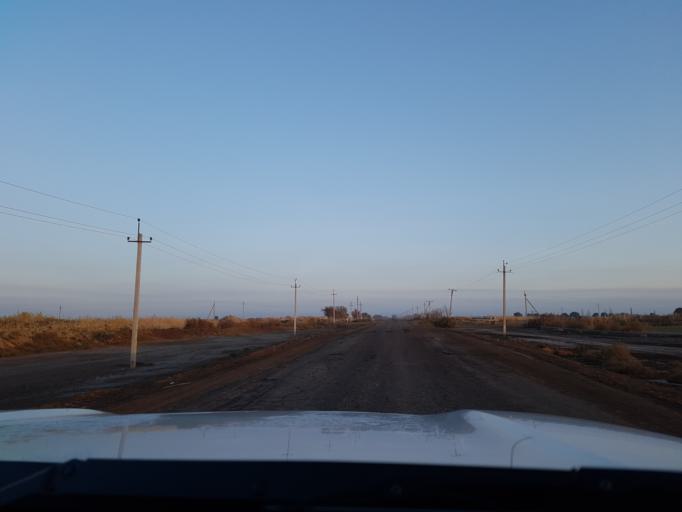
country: TM
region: Dasoguz
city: Koeneuergench
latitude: 41.8415
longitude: 58.7045
